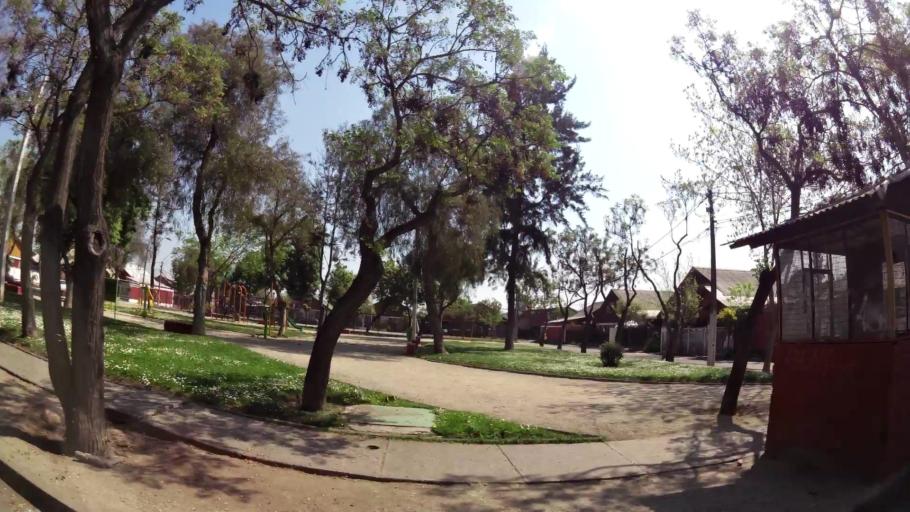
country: CL
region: Santiago Metropolitan
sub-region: Provincia de Santiago
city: La Pintana
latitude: -33.5485
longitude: -70.5995
